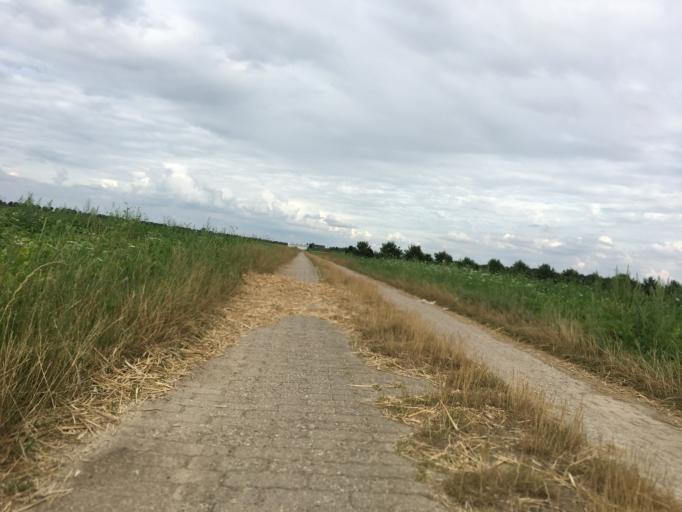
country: DE
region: North Rhine-Westphalia
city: Huckelhoven
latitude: 51.0855
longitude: 6.2336
